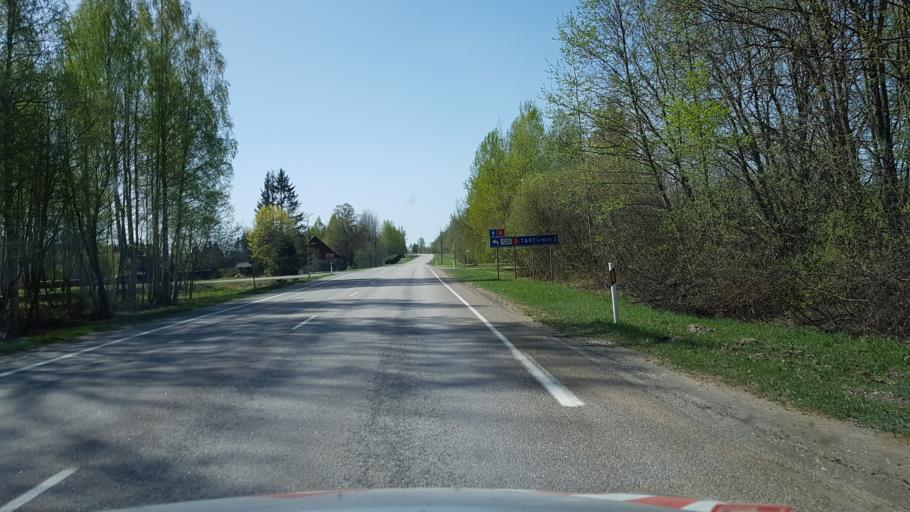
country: EE
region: Valgamaa
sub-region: Valga linn
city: Valga
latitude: 57.8068
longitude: 26.0397
